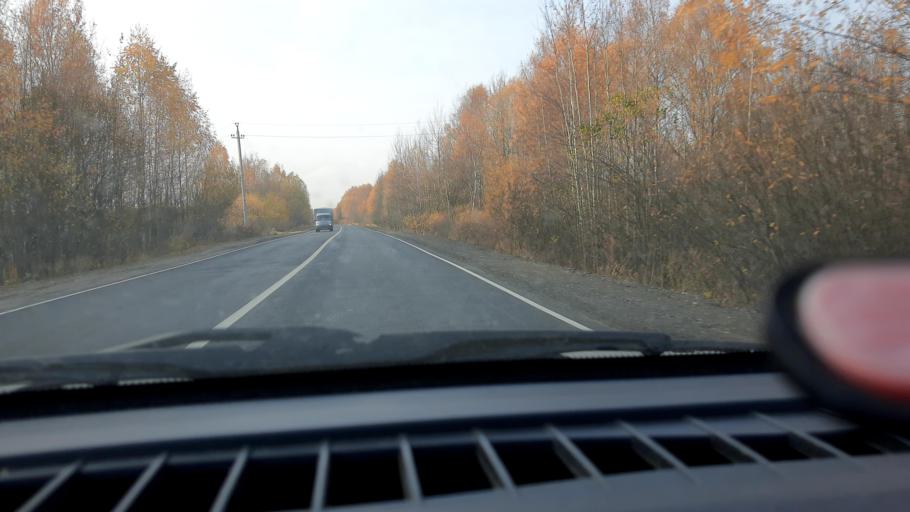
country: RU
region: Nizjnij Novgorod
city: Lukino
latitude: 56.5322
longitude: 43.8021
